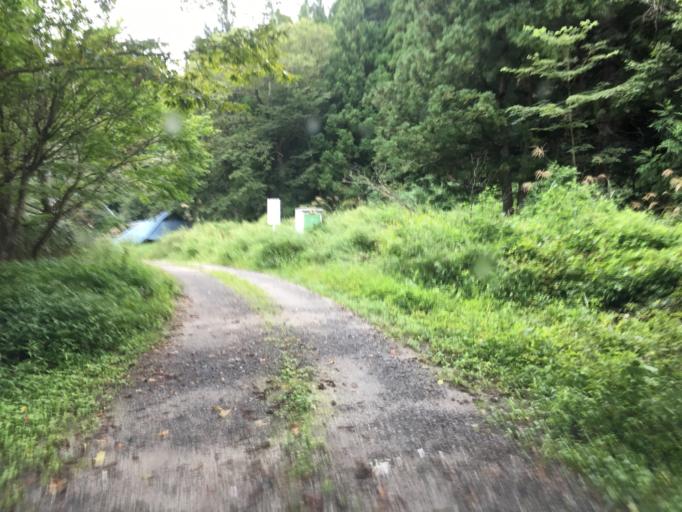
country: JP
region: Fukushima
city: Fukushima-shi
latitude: 37.8395
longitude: 140.3292
